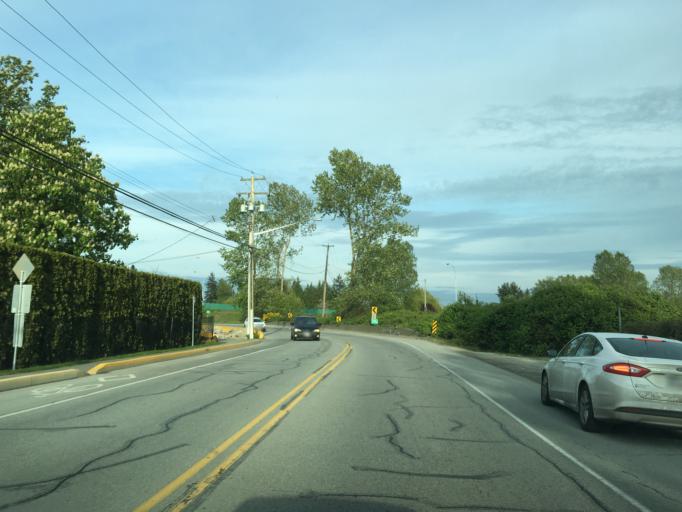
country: CA
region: British Columbia
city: New Westminster
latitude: 49.1818
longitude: -122.9628
